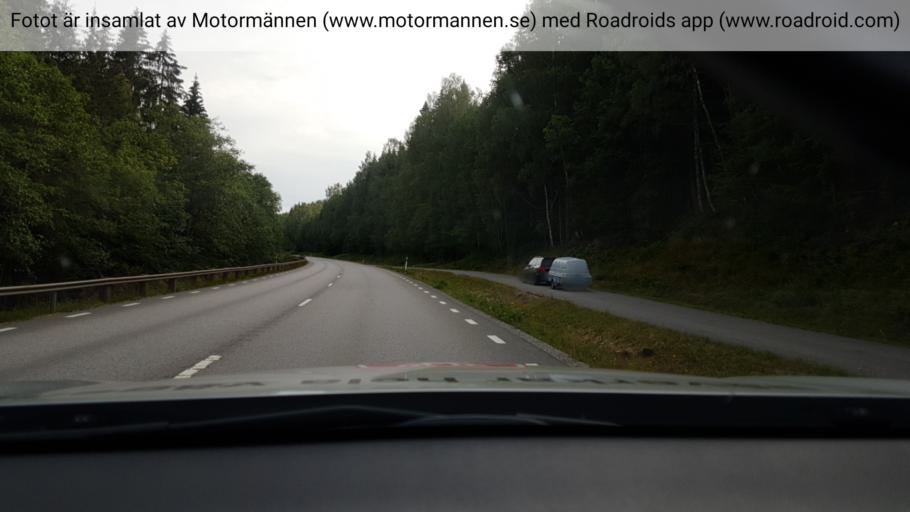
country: SE
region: Vaestra Goetaland
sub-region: Bengtsfors Kommun
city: Dals Langed
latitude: 59.0507
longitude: 12.4342
